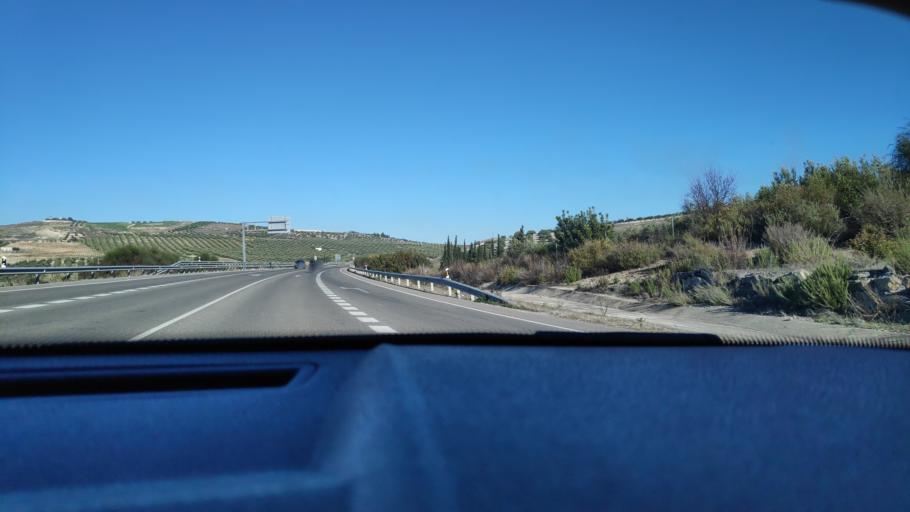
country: ES
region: Andalusia
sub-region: Province of Cordoba
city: Baena
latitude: 37.5983
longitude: -4.3037
